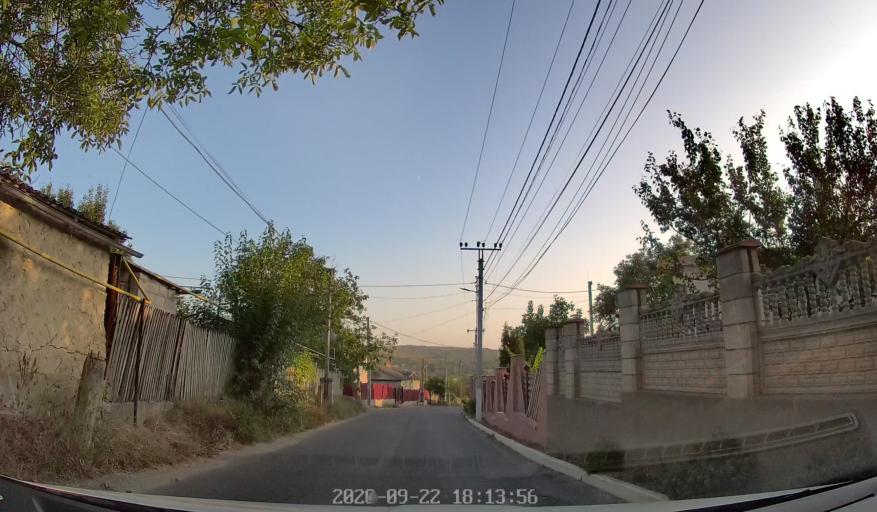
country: MD
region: Laloveni
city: Ialoveni
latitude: 46.9416
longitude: 28.7880
